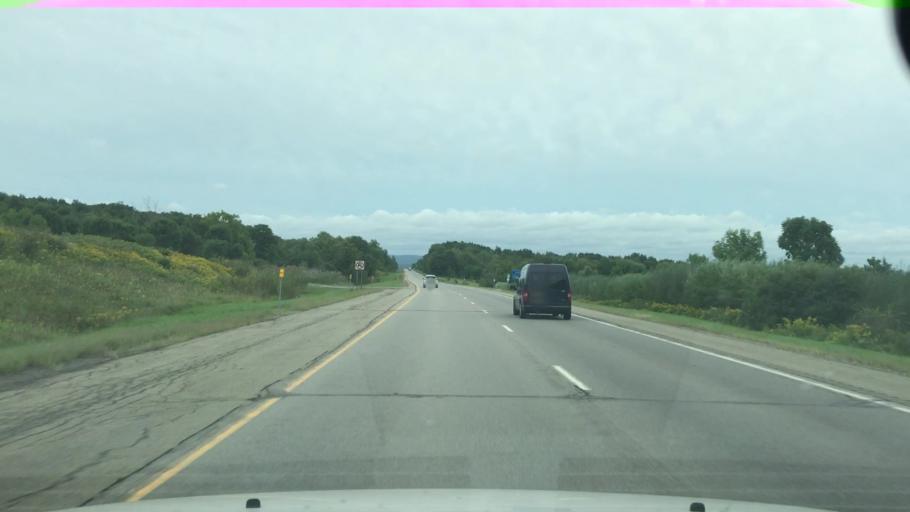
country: US
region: New York
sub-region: Erie County
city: Springville
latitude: 42.5392
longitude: -78.7087
